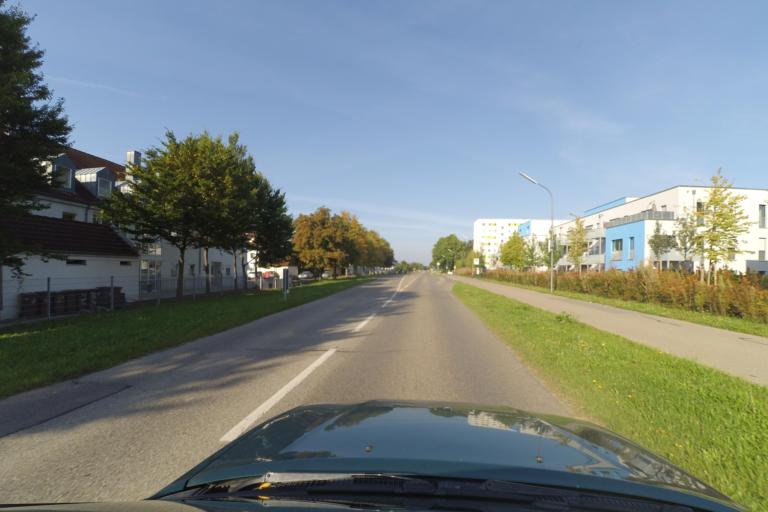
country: DE
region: Bavaria
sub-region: Upper Bavaria
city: Manching
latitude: 48.7164
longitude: 11.4752
